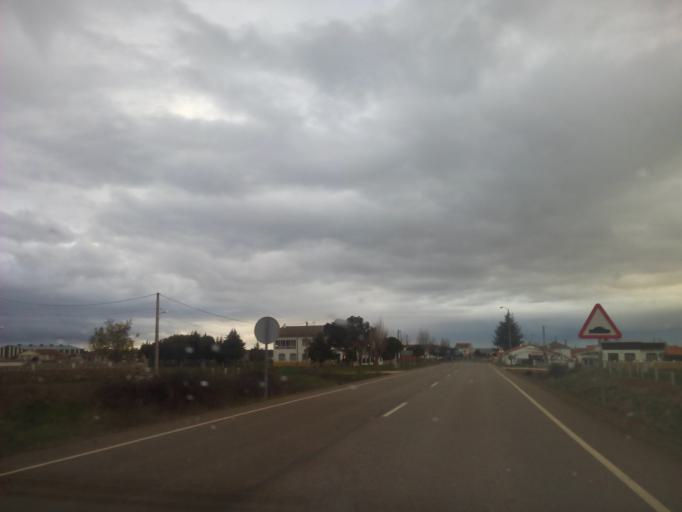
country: ES
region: Castille and Leon
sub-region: Provincia de Salamanca
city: Abusejo
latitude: 40.7064
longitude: -6.1403
